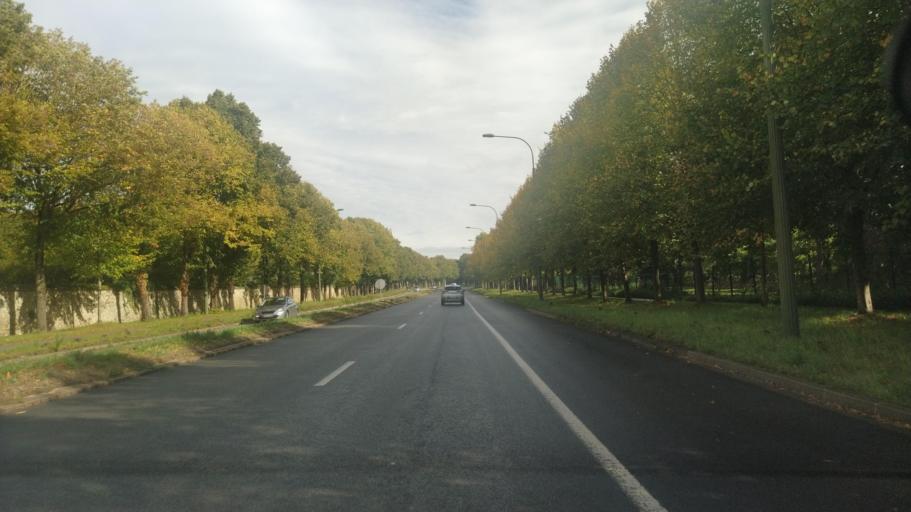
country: FR
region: Ile-de-France
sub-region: Departement des Yvelines
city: Le Chesnay
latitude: 48.8027
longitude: 2.1110
